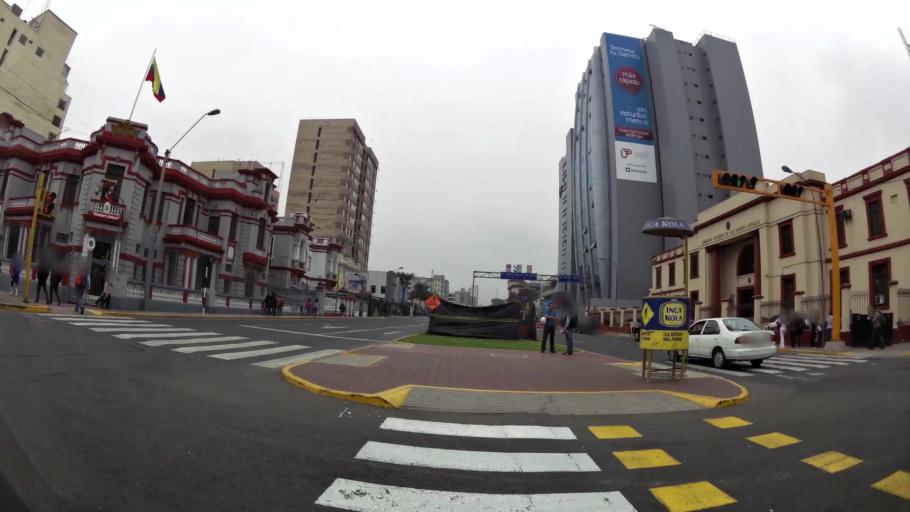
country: PE
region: Lima
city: Lima
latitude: -12.0671
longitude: -77.0371
